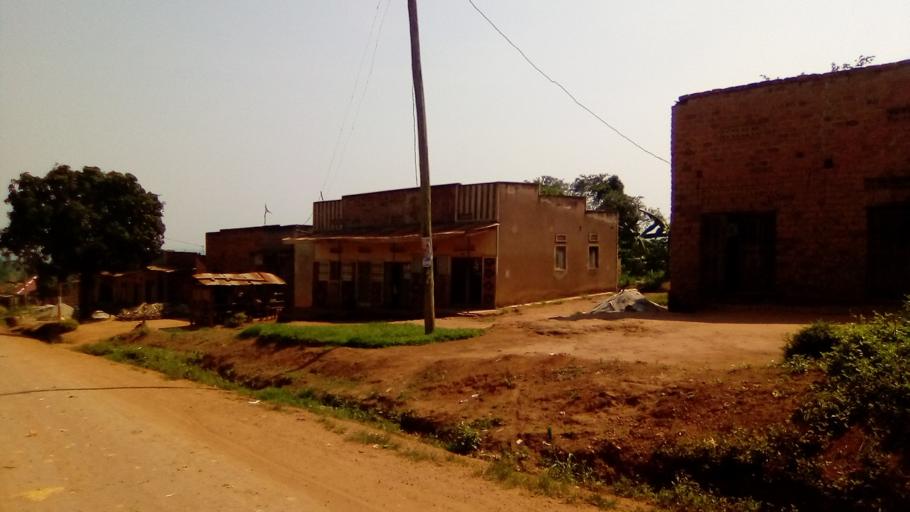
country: UG
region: Central Region
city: Masaka
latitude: -0.2707
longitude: 31.6458
